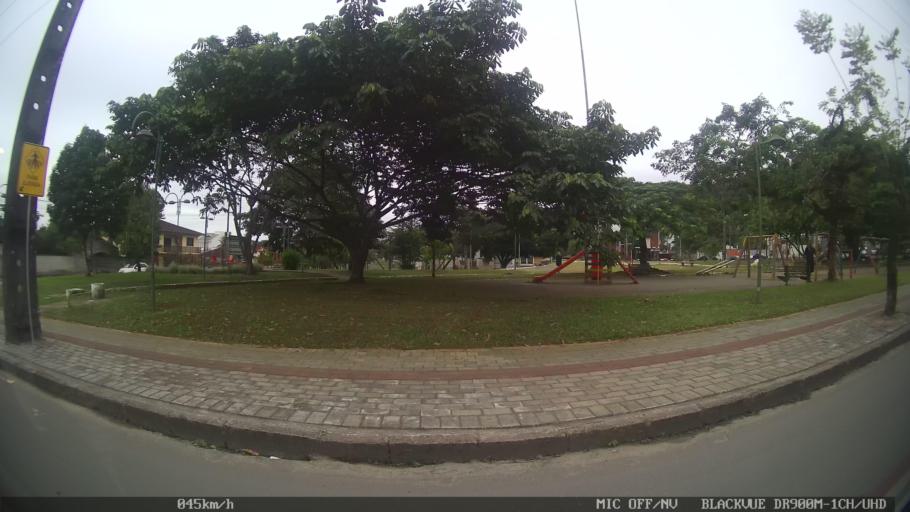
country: BR
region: Santa Catarina
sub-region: Joinville
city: Joinville
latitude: -26.2669
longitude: -48.8397
